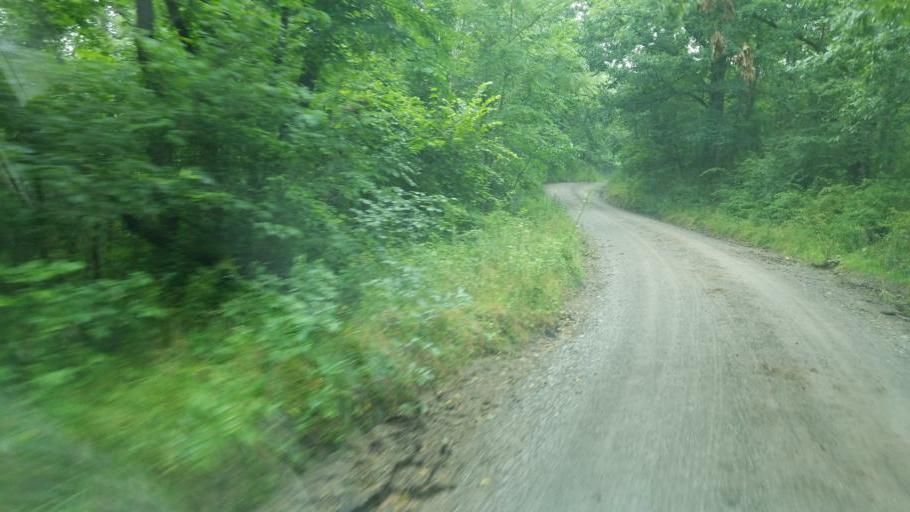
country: US
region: Ohio
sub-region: Columbiana County
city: Salineville
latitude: 40.5294
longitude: -80.8283
